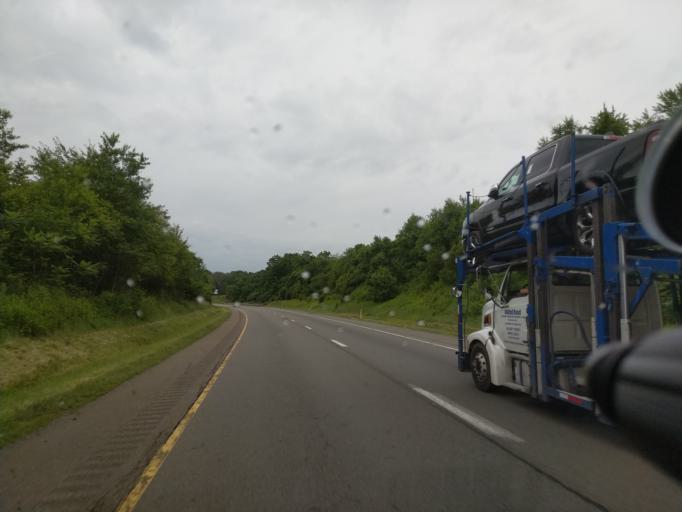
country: US
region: Pennsylvania
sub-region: Columbia County
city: Almedia
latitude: 41.0391
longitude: -76.3556
